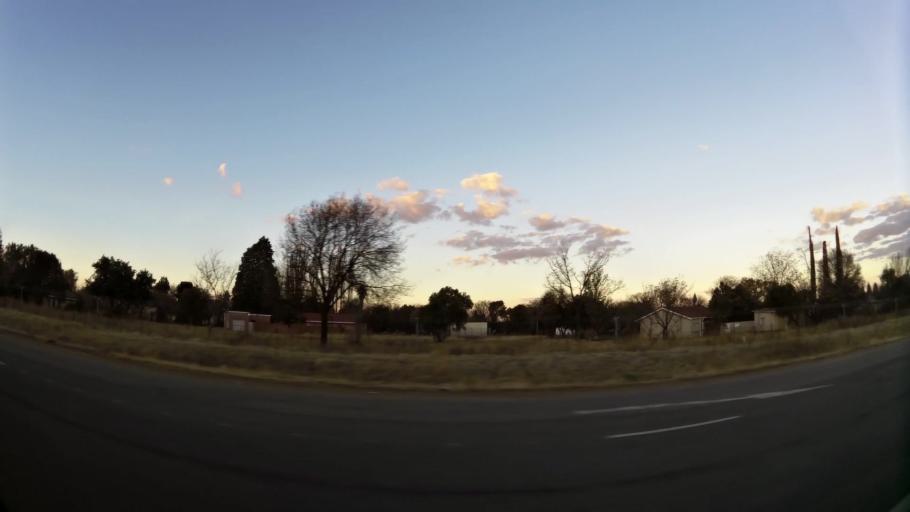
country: ZA
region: North-West
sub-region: Dr Kenneth Kaunda District Municipality
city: Potchefstroom
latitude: -26.6834
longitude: 27.0760
